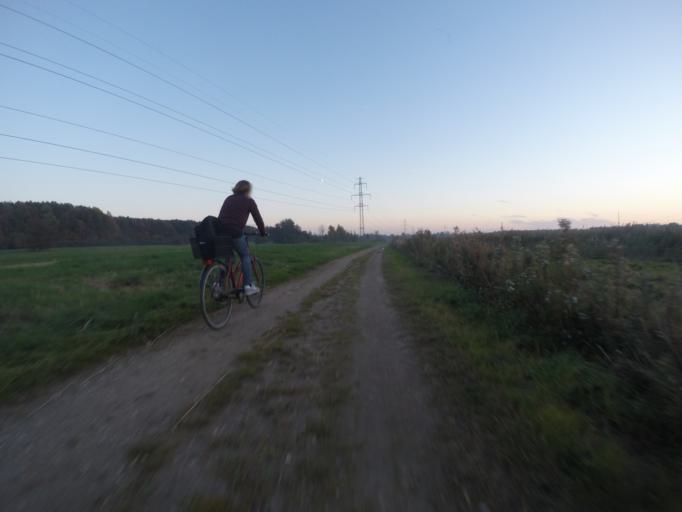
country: DK
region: Capital Region
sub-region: Hoje-Taastrup Kommune
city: Taastrup
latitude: 55.6679
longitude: 12.3195
